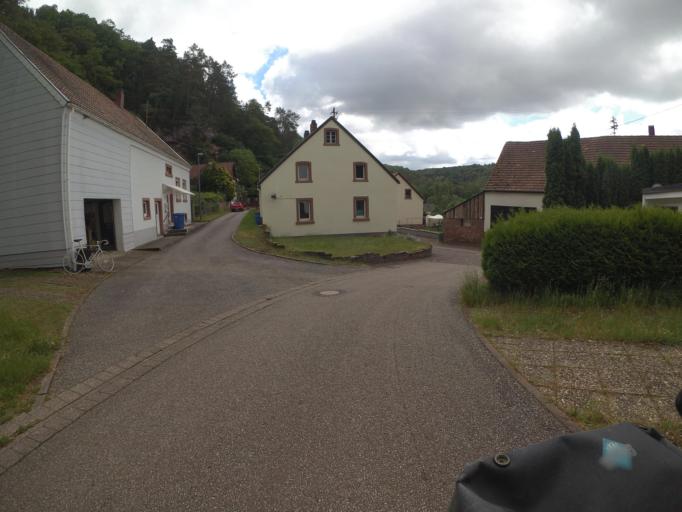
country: DE
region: Rheinland-Pfalz
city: Trulben
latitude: 49.1309
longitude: 7.5445
